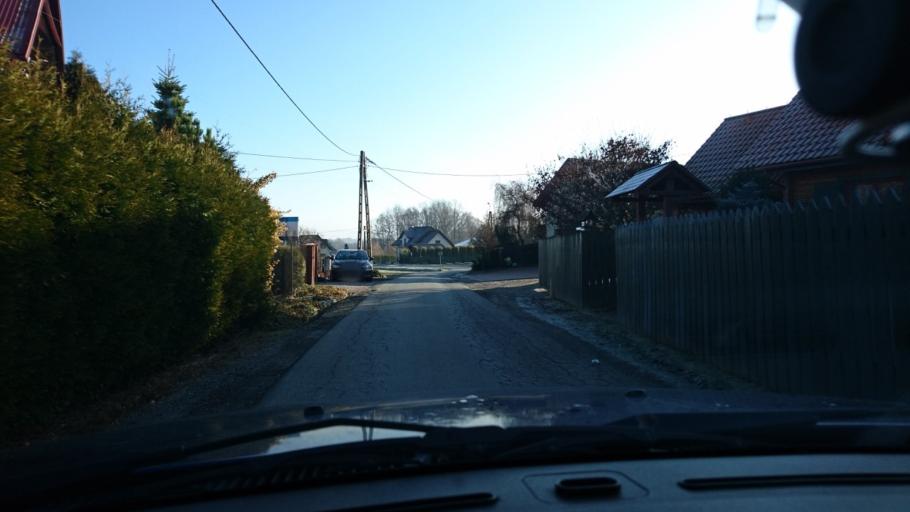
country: PL
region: Silesian Voivodeship
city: Janowice
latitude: 49.8923
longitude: 19.1146
